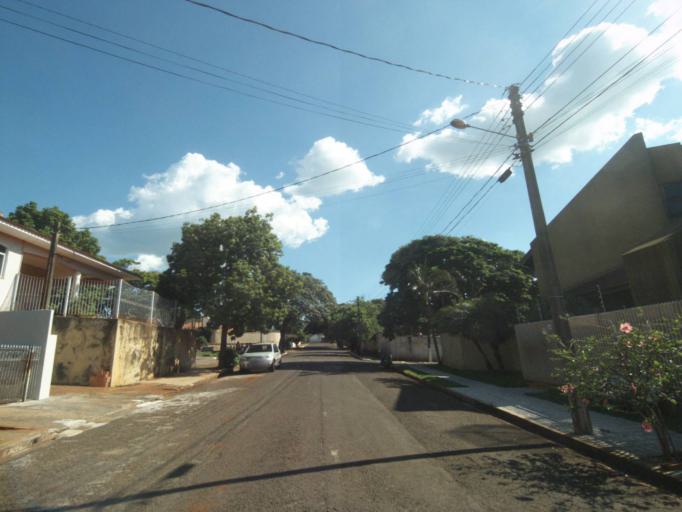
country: BR
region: Parana
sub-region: Sertanopolis
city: Sertanopolis
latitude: -23.0408
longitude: -50.8160
